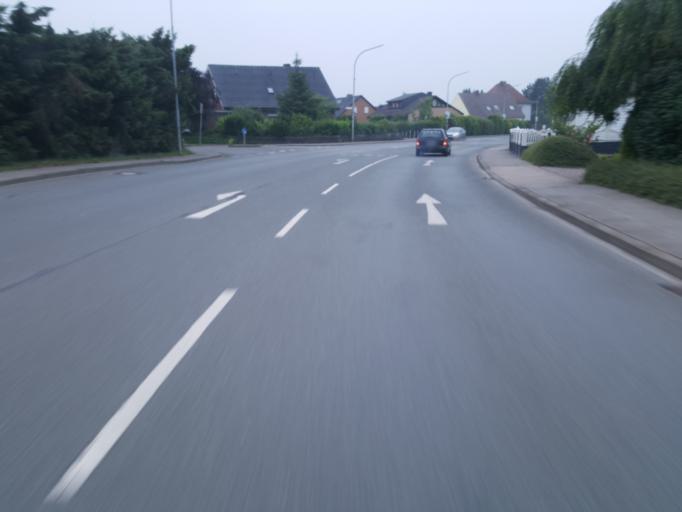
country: DE
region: North Rhine-Westphalia
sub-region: Regierungsbezirk Detmold
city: Kirchlengern
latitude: 52.1914
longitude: 8.6450
